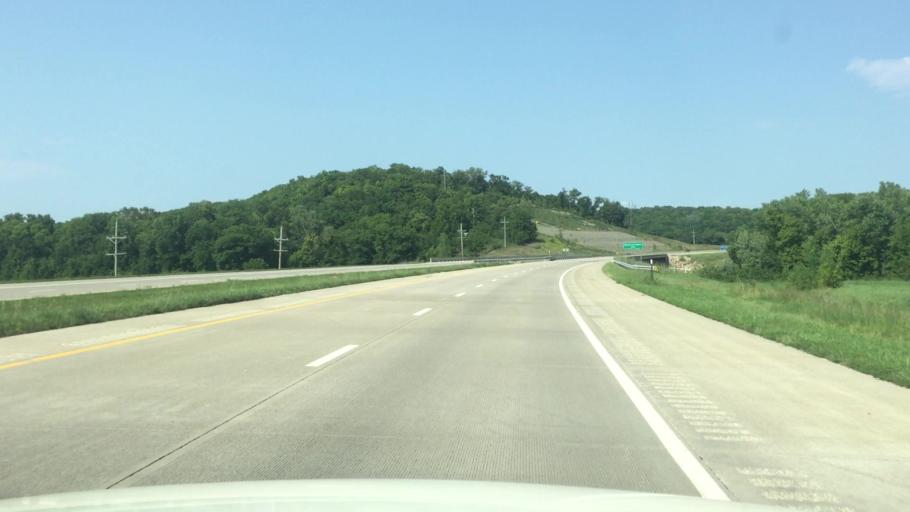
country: US
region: Kansas
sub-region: Linn County
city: Pleasanton
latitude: 38.2470
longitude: -94.6875
